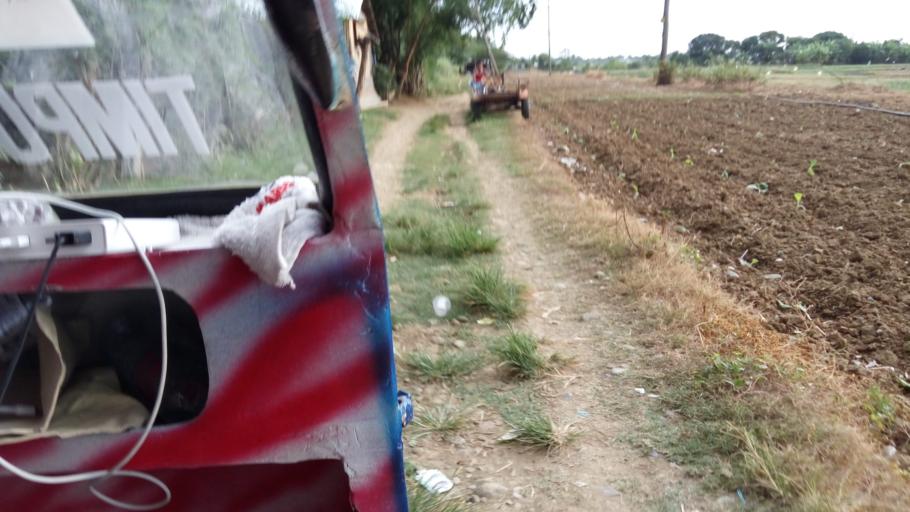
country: PH
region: Ilocos
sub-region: Province of La Union
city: Santo Tomas
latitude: 16.2763
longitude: 120.3879
